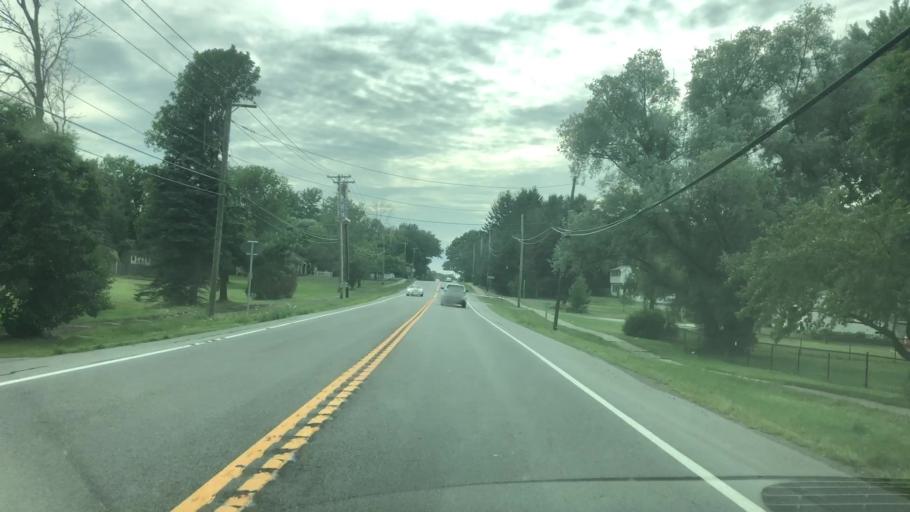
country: US
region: New York
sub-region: Monroe County
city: Fairport
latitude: 43.1306
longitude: -77.4270
